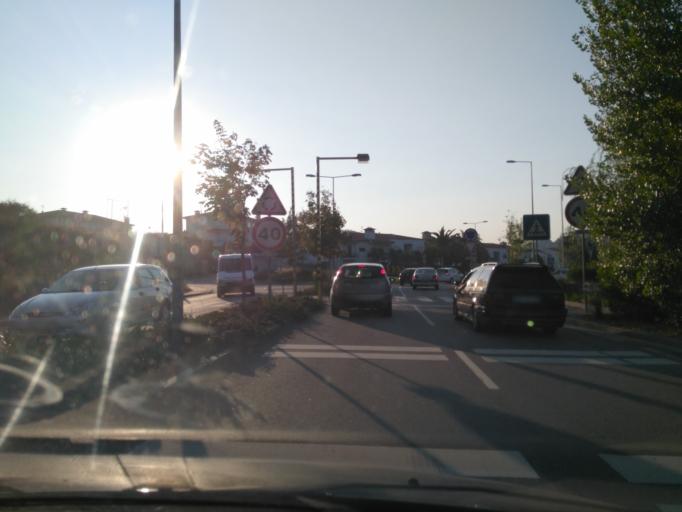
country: PT
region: Braga
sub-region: Guimaraes
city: Brito
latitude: 41.4476
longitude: -8.3434
